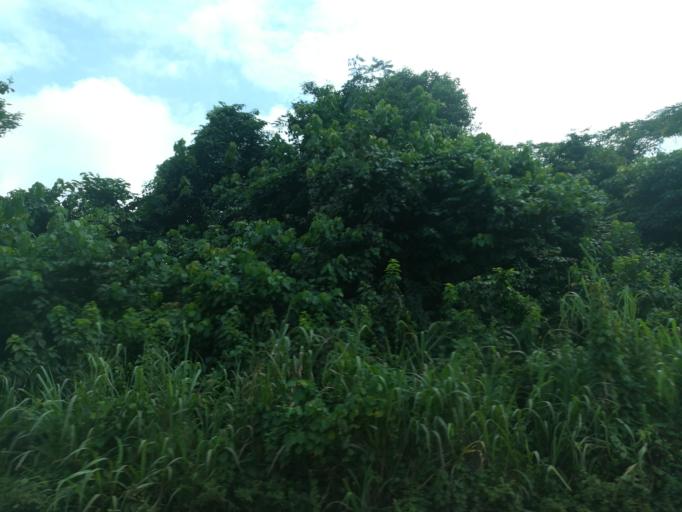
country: NG
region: Lagos
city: Ikorodu
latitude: 6.6725
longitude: 3.6595
